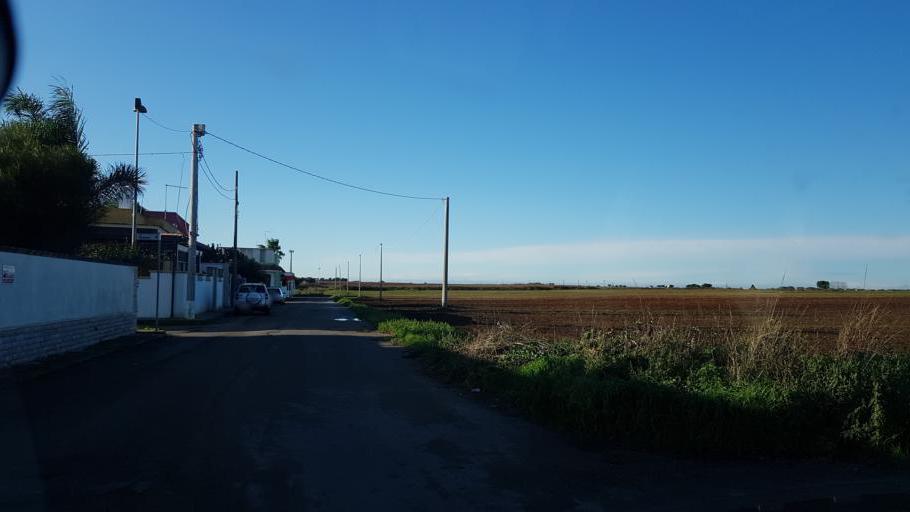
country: IT
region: Apulia
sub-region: Provincia di Brindisi
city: Torchiarolo
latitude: 40.5359
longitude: 18.0714
